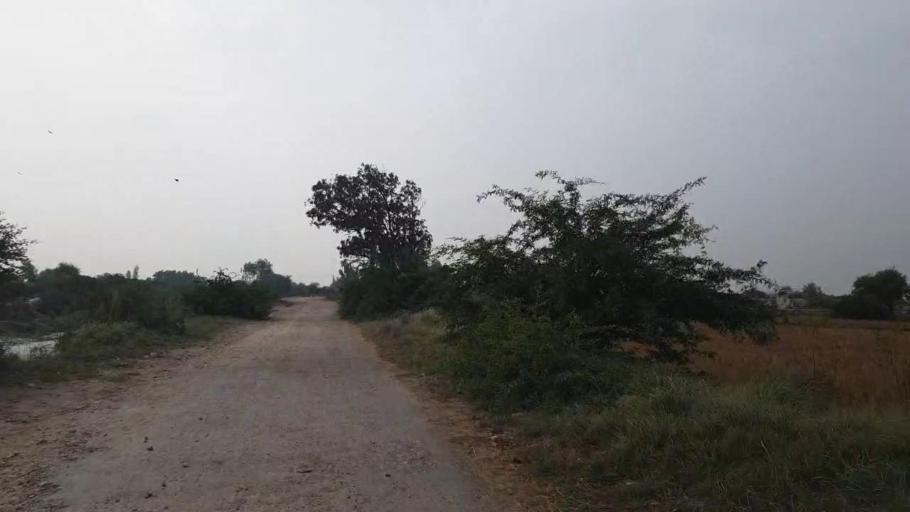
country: PK
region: Sindh
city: Kario
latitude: 24.8832
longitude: 68.5257
